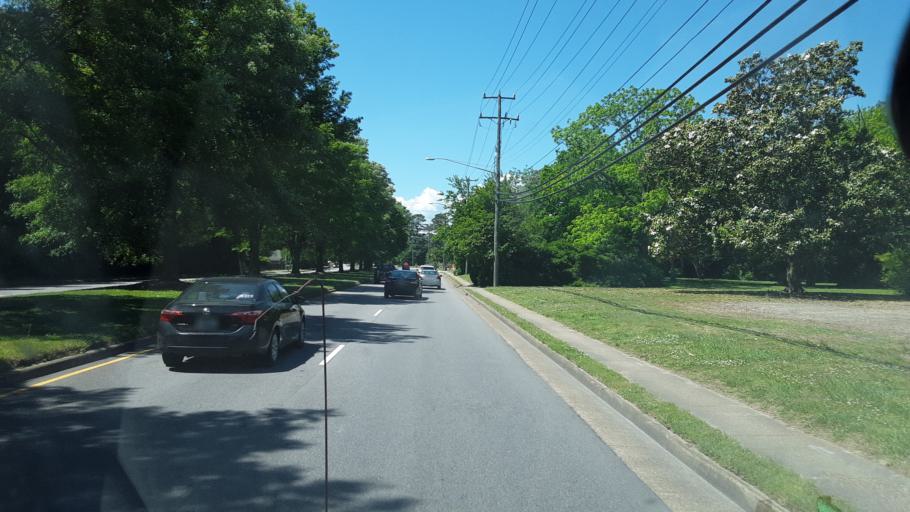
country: US
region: Virginia
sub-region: City of Virginia Beach
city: Virginia Beach
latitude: 36.7745
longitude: -76.0074
